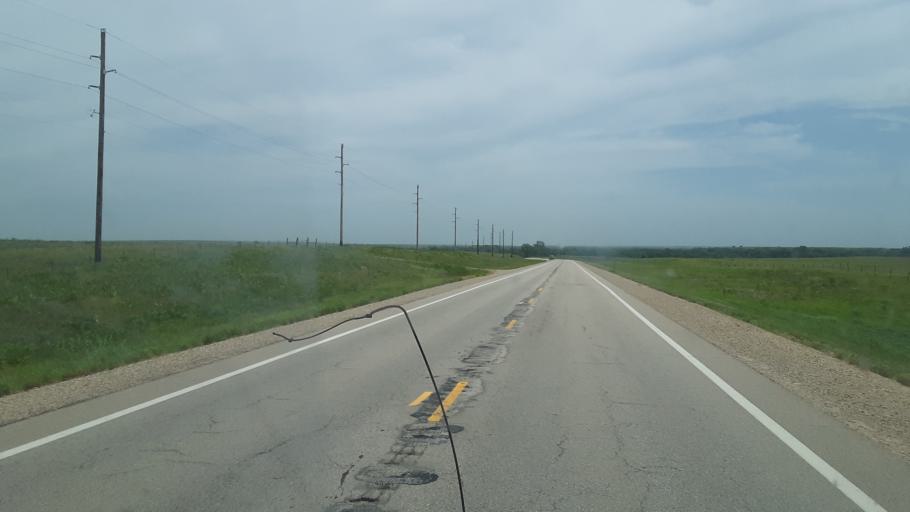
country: US
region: Kansas
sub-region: Greenwood County
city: Eureka
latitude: 37.8378
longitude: -96.1210
